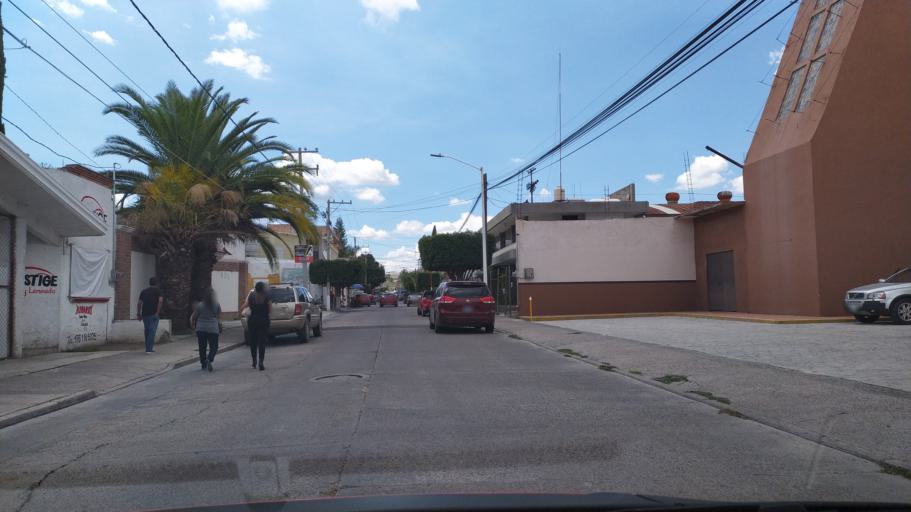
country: MX
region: Guanajuato
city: San Francisco del Rincon
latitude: 21.0300
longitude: -101.8584
